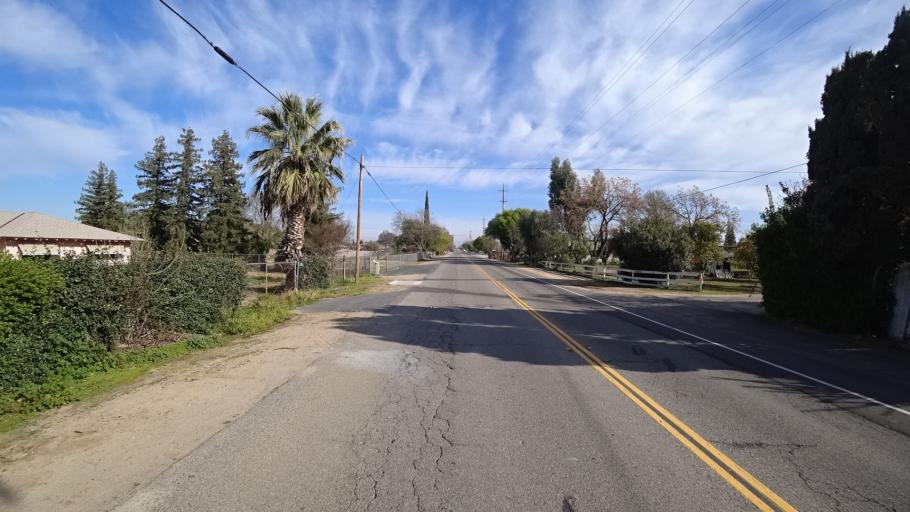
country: US
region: California
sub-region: Fresno County
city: West Park
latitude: 36.7684
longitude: -119.8804
